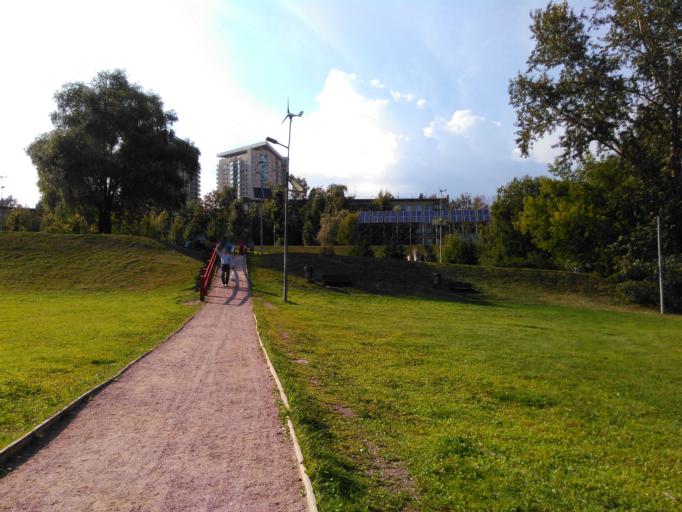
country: RU
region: Moscow
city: Davydkovo
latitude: 55.7133
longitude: 37.4636
